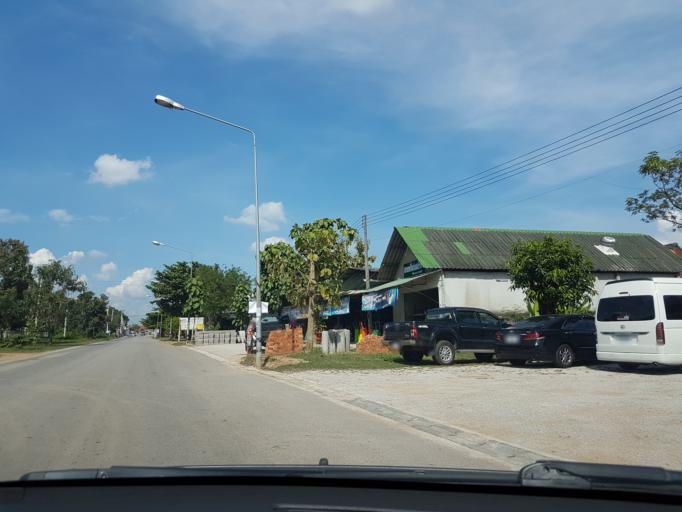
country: TH
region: Lampang
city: Ko Kha
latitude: 18.2135
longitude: 99.3898
